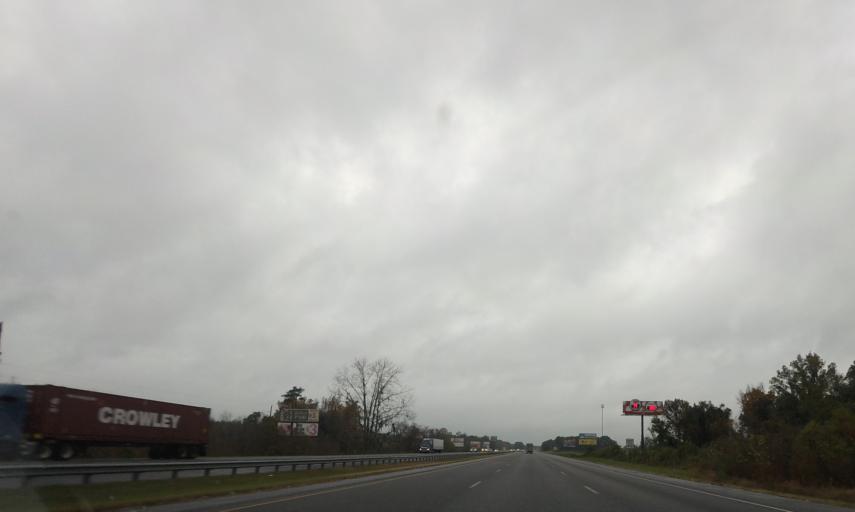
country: US
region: Georgia
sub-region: Echols County
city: Statenville
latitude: 30.6540
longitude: -83.1987
